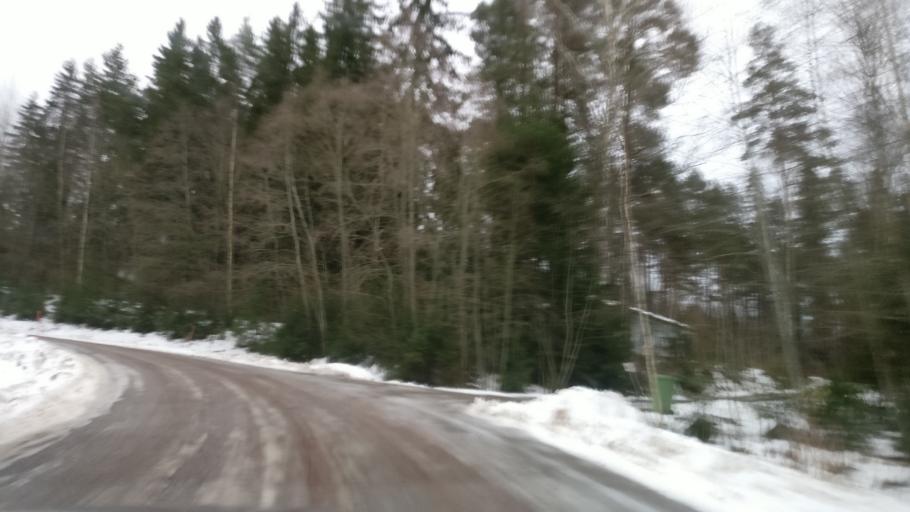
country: FI
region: Uusimaa
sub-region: Raaseporin
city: Karis
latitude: 60.0702
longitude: 23.8054
